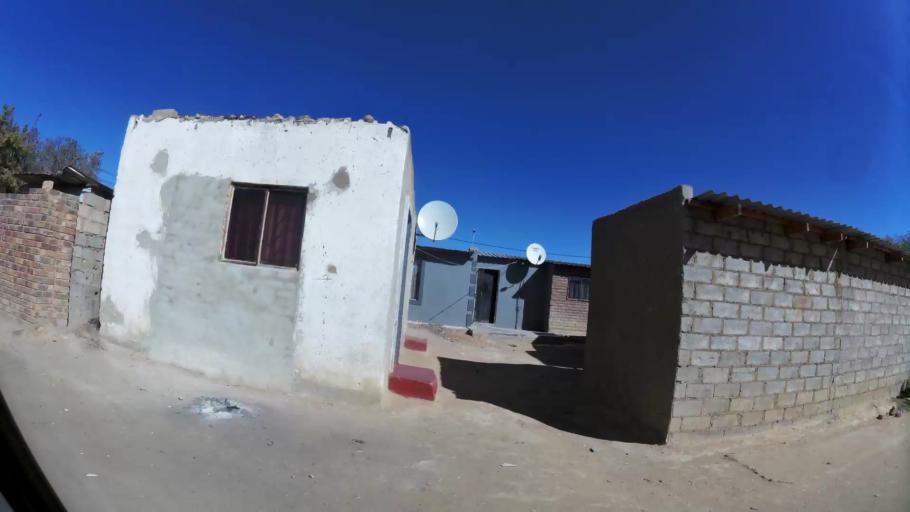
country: ZA
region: Gauteng
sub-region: City of Johannesburg Metropolitan Municipality
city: Midrand
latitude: -25.9197
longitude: 28.0918
